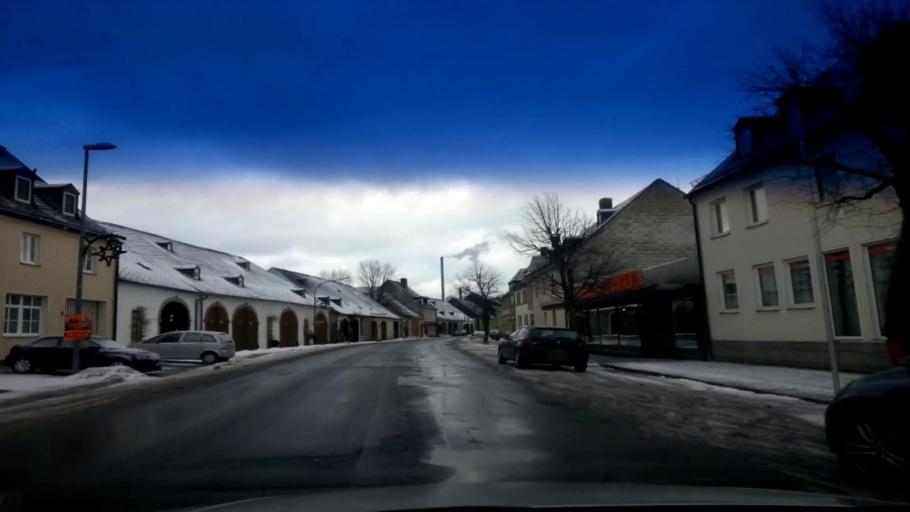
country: DE
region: Bavaria
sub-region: Upper Franconia
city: Weissenstadt
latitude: 50.1035
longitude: 11.8866
